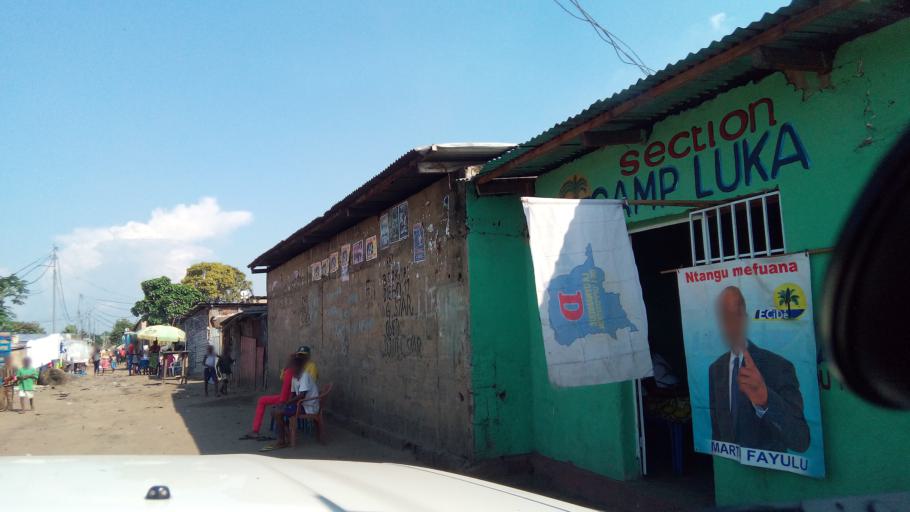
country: CD
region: Kinshasa
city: Kinshasa
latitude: -4.3688
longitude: 15.2735
